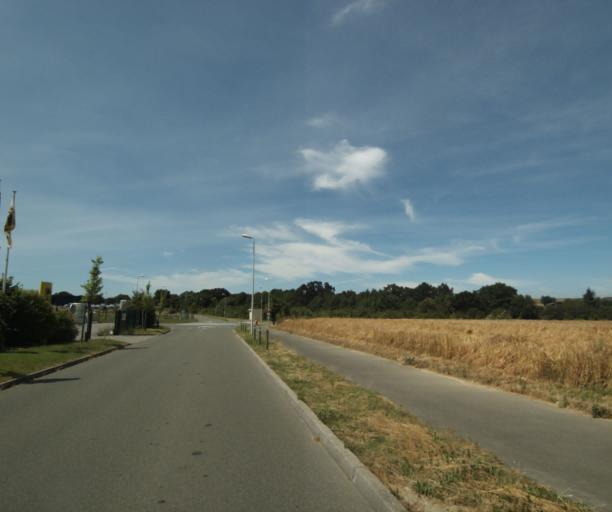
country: FR
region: Pays de la Loire
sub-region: Departement de la Mayenne
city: Change
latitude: 48.0865
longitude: -0.8044
